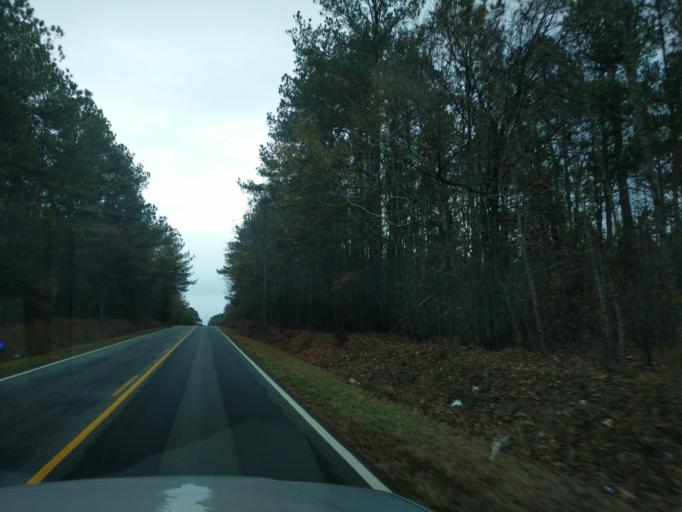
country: US
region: South Carolina
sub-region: Laurens County
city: Laurens
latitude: 34.3785
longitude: -82.0047
